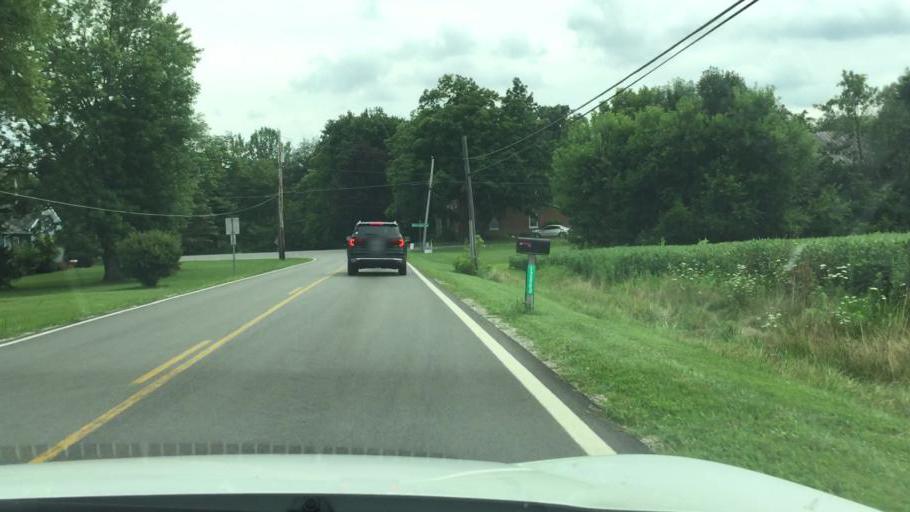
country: US
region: Ohio
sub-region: Union County
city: Marysville
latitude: 40.1840
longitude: -83.4381
